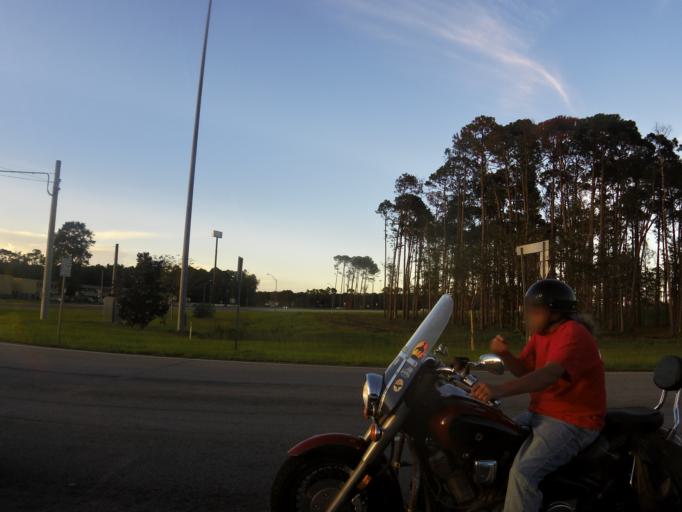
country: US
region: Georgia
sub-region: Camden County
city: Kingsland
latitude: 30.7916
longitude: -81.6615
